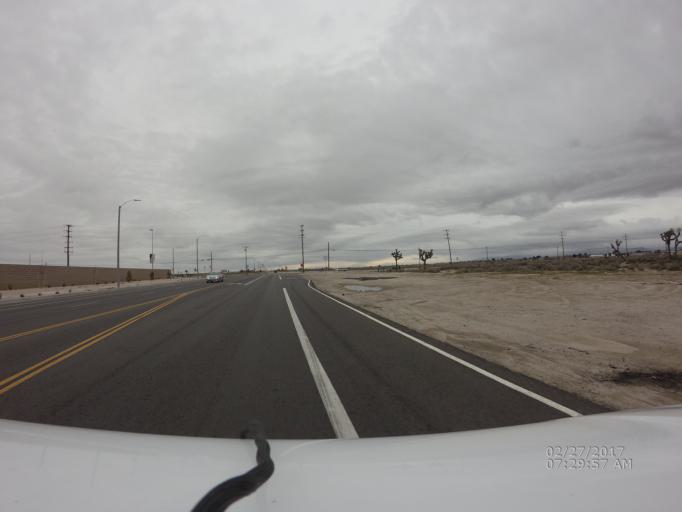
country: US
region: California
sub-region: Los Angeles County
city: Lancaster
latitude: 34.7187
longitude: -118.1316
